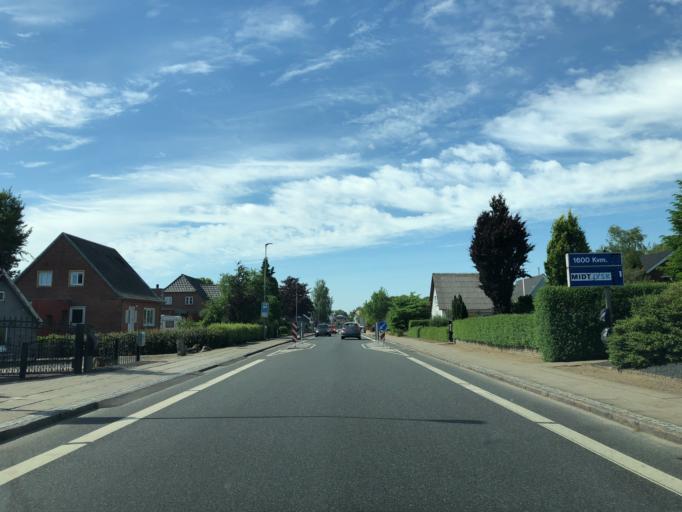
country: DK
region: Central Jutland
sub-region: Ikast-Brande Kommune
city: Brande
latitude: 55.9395
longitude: 9.1329
